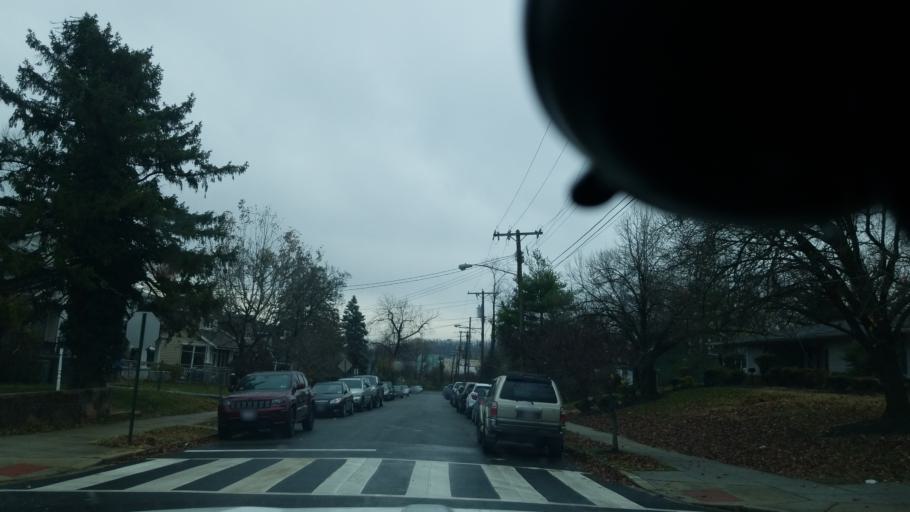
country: US
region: Maryland
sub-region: Prince George's County
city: Mount Rainier
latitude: 38.9246
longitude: -76.9722
